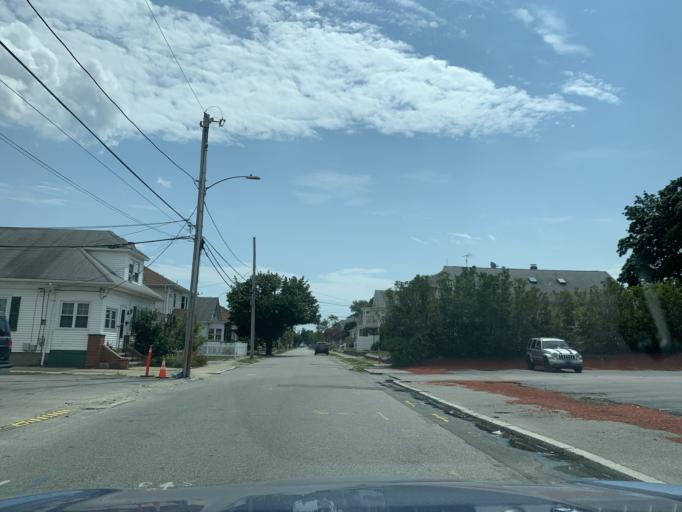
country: US
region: Rhode Island
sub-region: Providence County
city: Cranston
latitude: 41.7837
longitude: -71.4373
